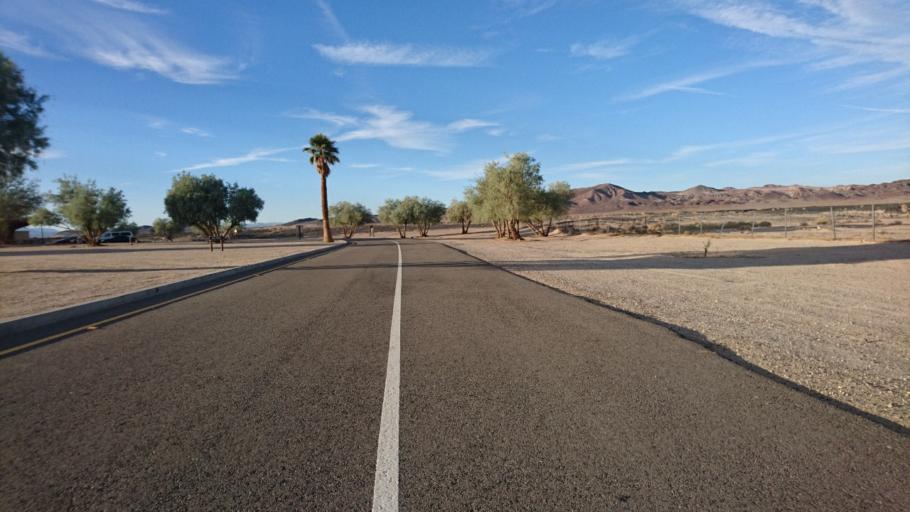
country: US
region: California
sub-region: San Bernardino County
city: Fort Irwin
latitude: 34.8012
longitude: -116.5203
